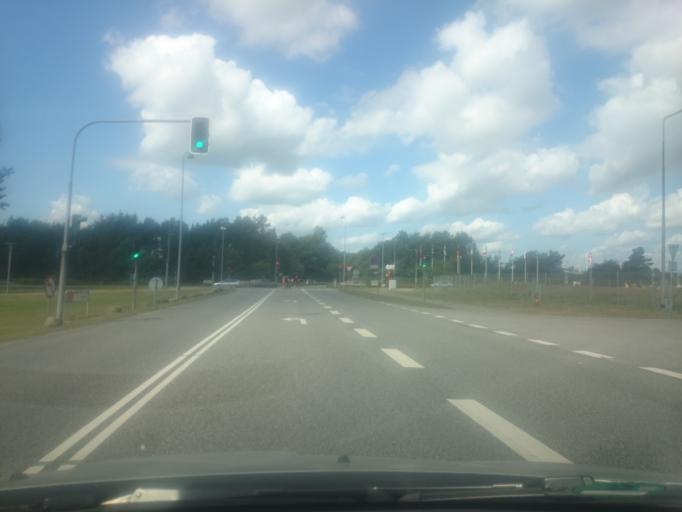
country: DK
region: South Denmark
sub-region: Billund Kommune
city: Billund
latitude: 55.7339
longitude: 9.1353
